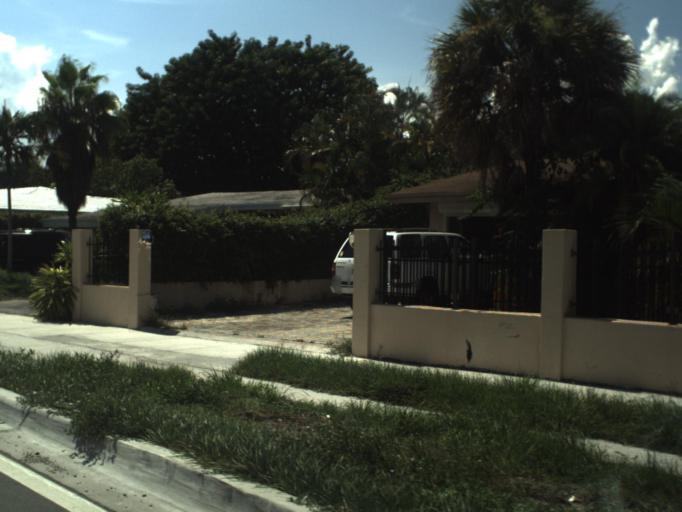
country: US
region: Florida
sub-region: Miami-Dade County
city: Ojus
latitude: 25.9471
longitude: -80.1574
